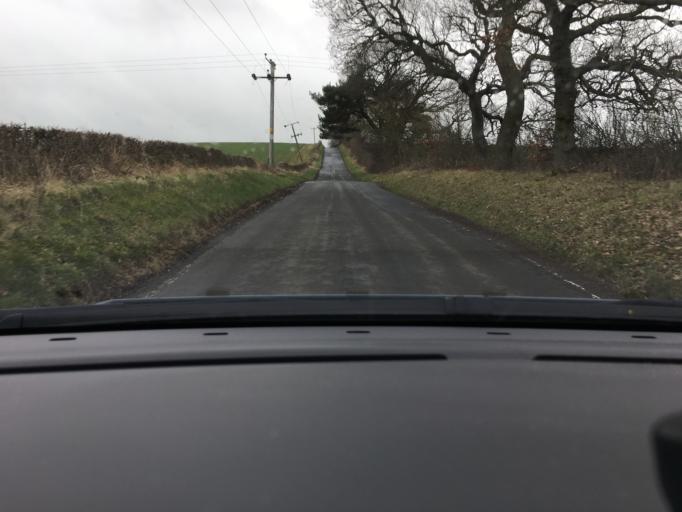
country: GB
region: Scotland
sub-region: West Lothian
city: Linlithgow
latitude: 55.9619
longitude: -3.5545
